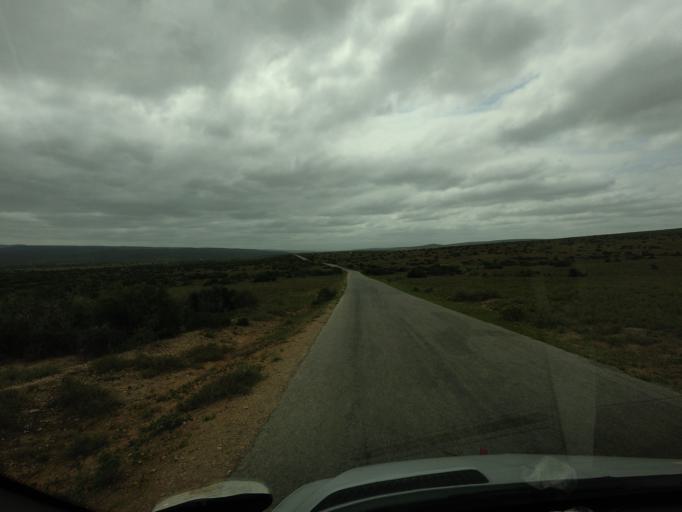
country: ZA
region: Eastern Cape
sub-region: Cacadu District Municipality
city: Kirkwood
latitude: -33.4397
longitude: 25.7694
